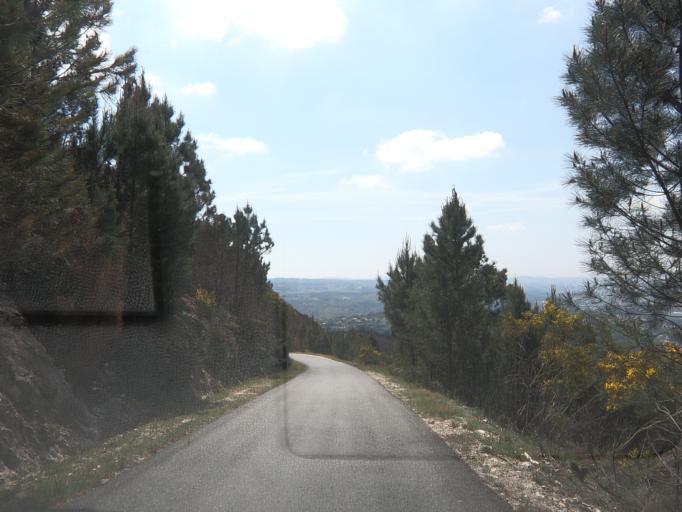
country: PT
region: Vila Real
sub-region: Vila Real
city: Vila Real
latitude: 41.3547
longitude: -7.7371
